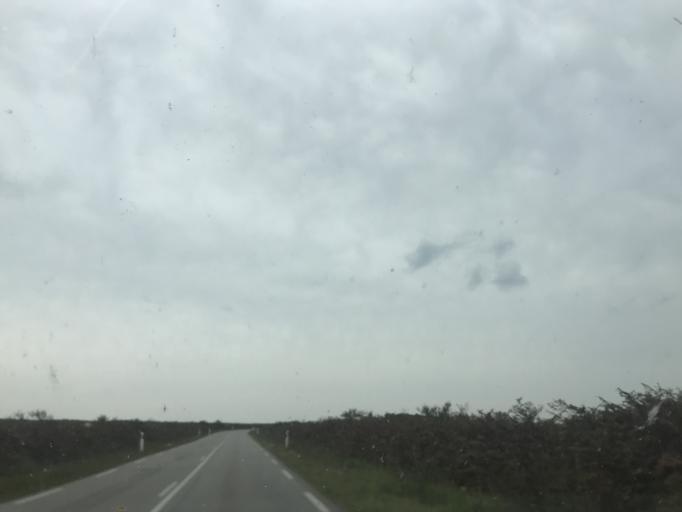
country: FR
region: Brittany
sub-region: Departement du Finistere
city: Plouneour-Menez
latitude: 48.3909
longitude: -3.9352
